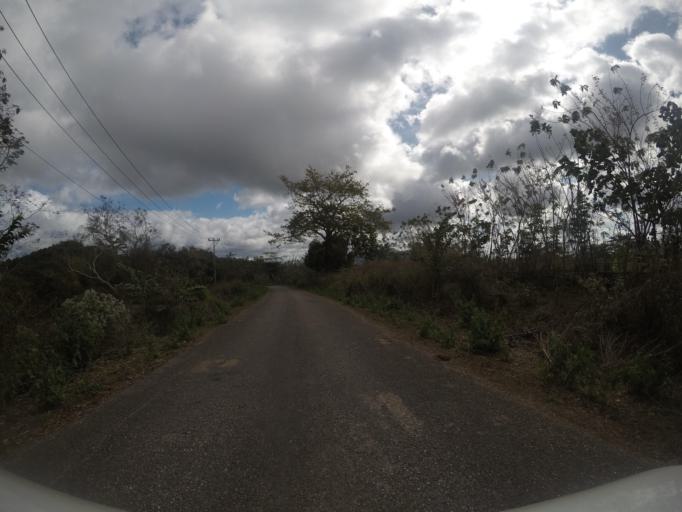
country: TL
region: Lautem
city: Lospalos
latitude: -8.5376
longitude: 126.9081
